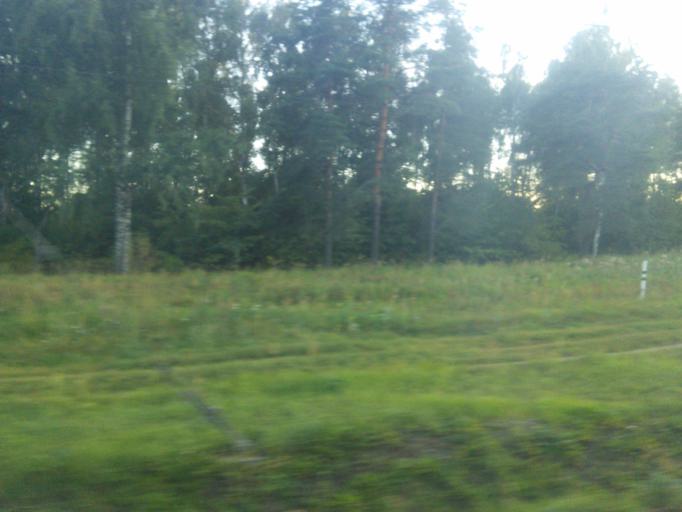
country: RU
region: Moskovskaya
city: Kupavna
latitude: 55.7403
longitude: 38.1666
